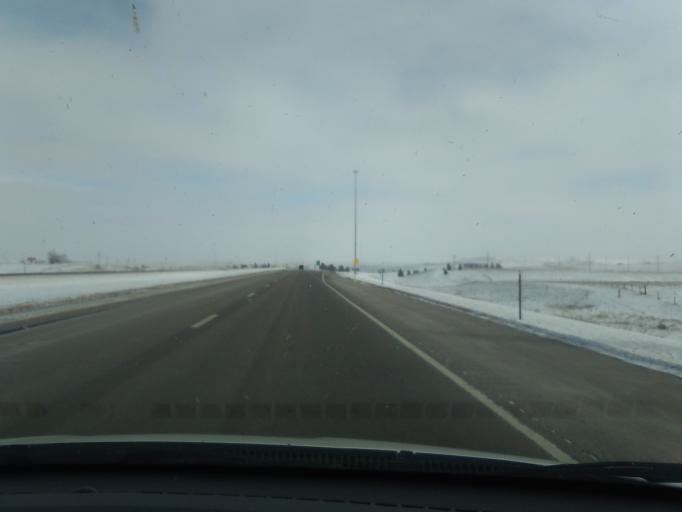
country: US
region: Nebraska
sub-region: Kimball County
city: Kimball
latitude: 41.2152
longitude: -103.6736
